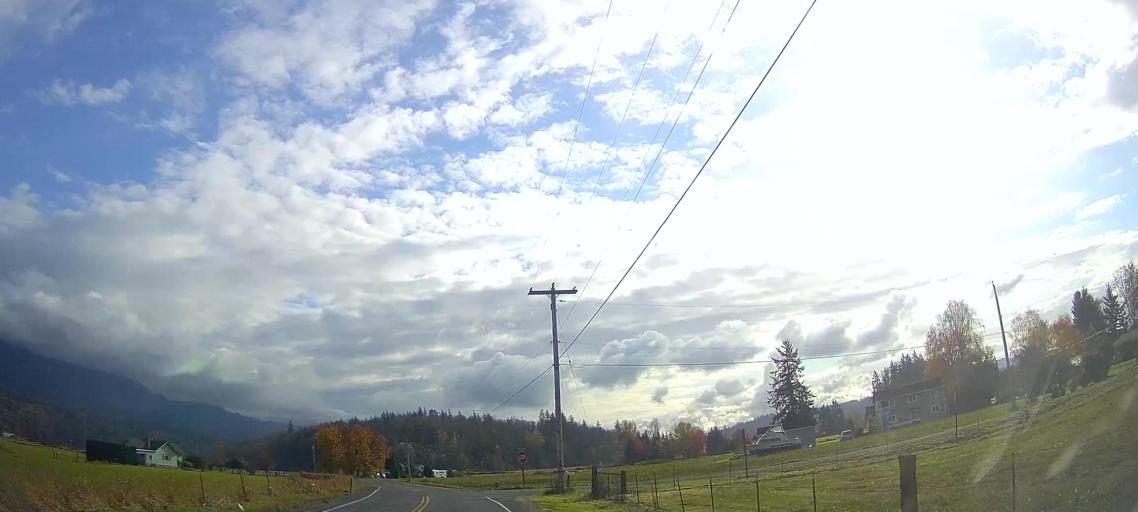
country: US
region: Washington
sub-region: Skagit County
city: Clear Lake
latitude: 48.4540
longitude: -122.2328
